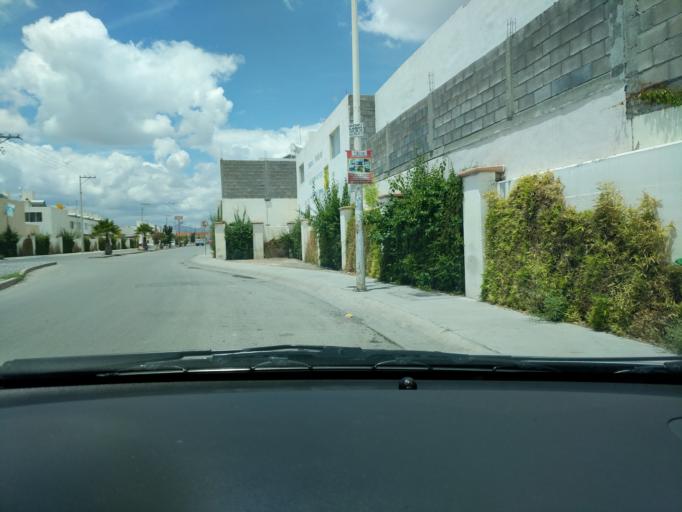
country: MX
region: San Luis Potosi
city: Soledad Diez Gutierrez
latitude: 22.2170
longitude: -100.9365
